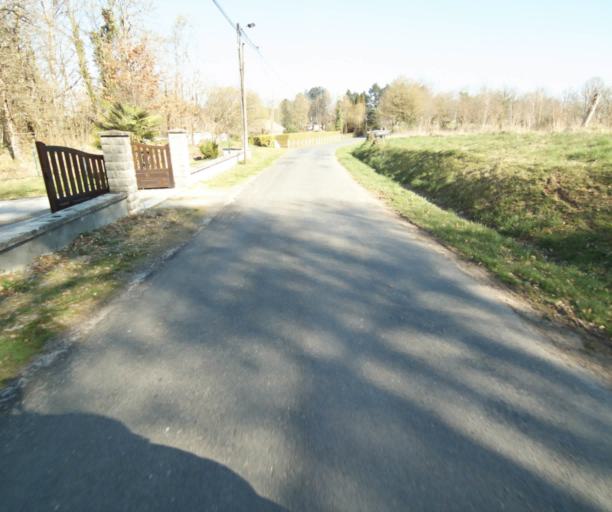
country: FR
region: Limousin
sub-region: Departement de la Correze
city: Chameyrat
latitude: 45.2822
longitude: 1.7164
